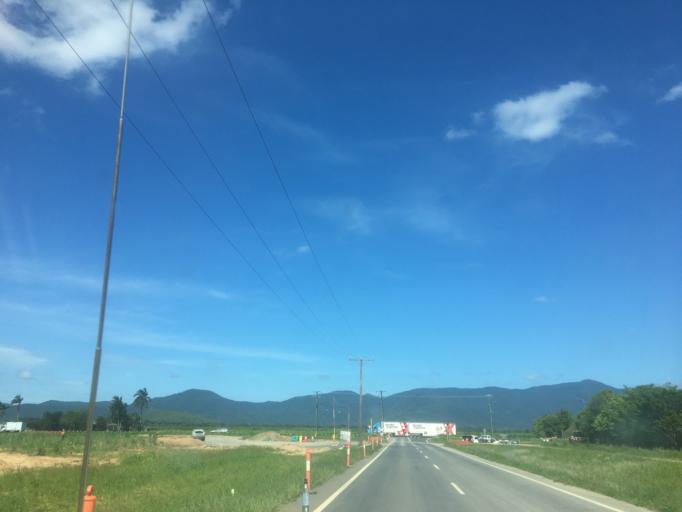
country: AU
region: Queensland
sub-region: Cairns
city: Woree
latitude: -17.0603
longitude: 145.7678
